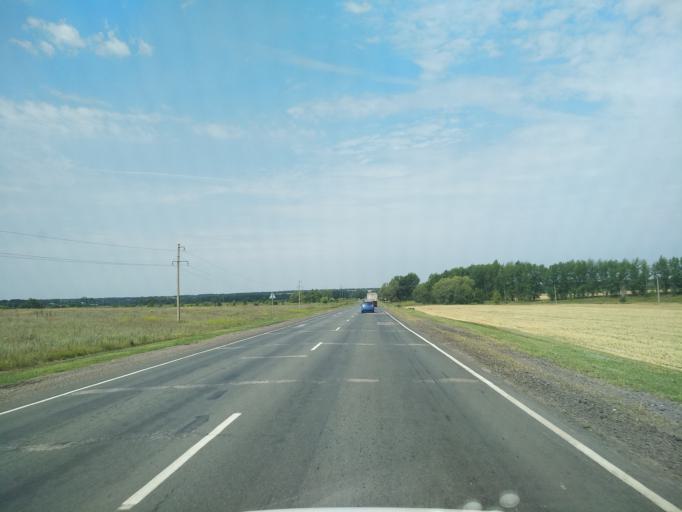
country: RU
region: Voronezj
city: Orlovo
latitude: 51.6800
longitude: 39.6175
